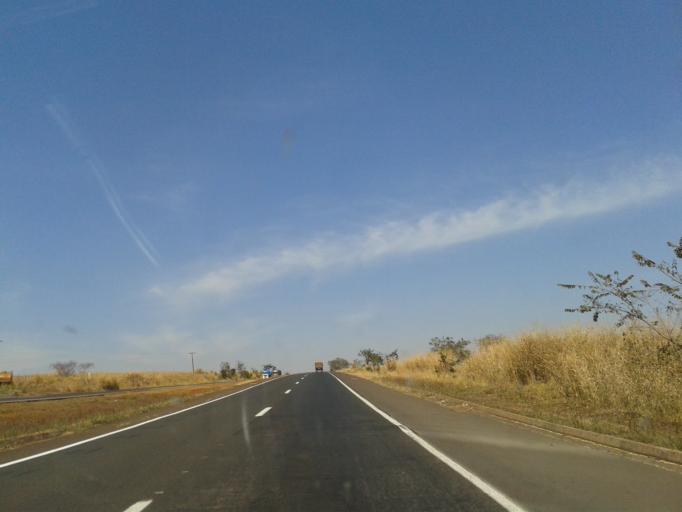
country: BR
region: Goias
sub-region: Goiatuba
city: Goiatuba
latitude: -18.1595
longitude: -49.2877
